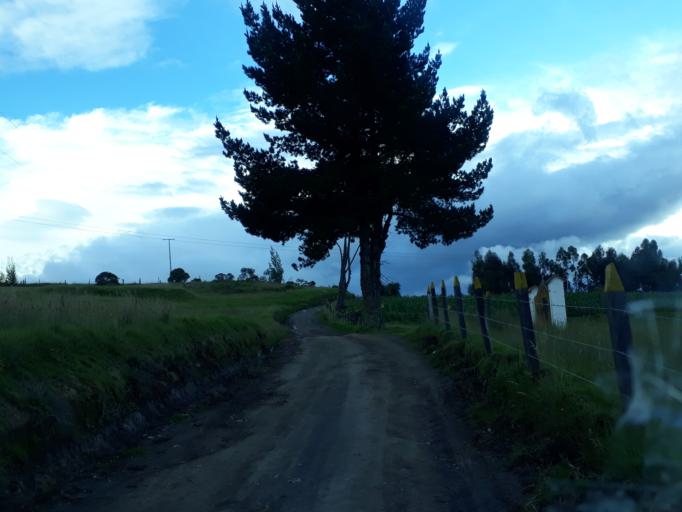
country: CO
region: Cundinamarca
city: Carmen de Carupa
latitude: 5.3304
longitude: -73.9107
